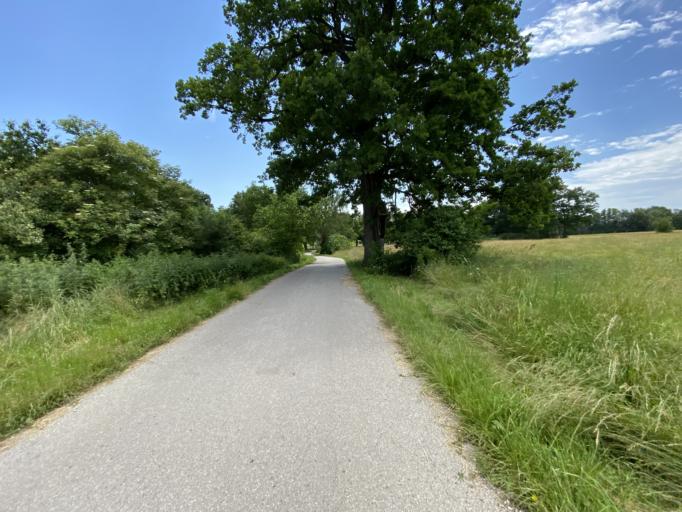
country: DE
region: Bavaria
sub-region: Upper Bavaria
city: Seefeld
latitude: 48.0500
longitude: 11.2226
